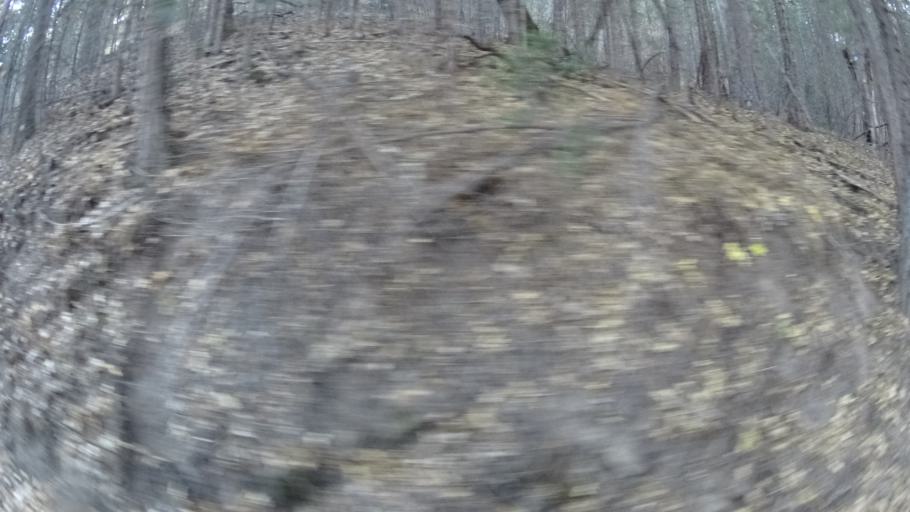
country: US
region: California
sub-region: Siskiyou County
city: Yreka
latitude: 41.8397
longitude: -122.8741
